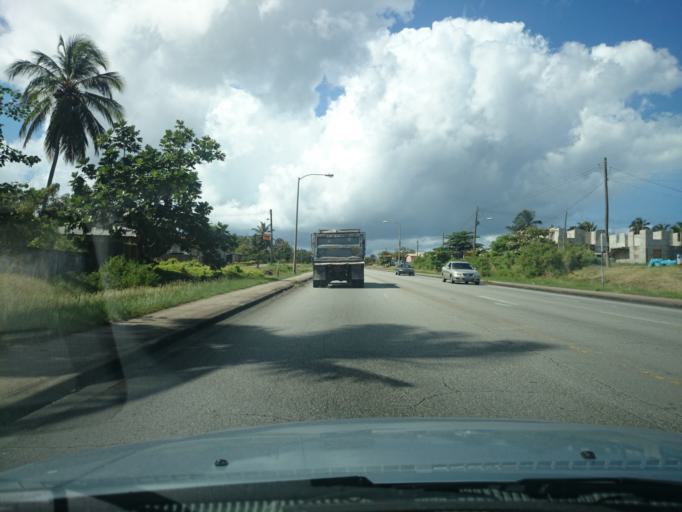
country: BB
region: Saint Michael
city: Bridgetown
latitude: 13.1399
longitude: -59.6155
